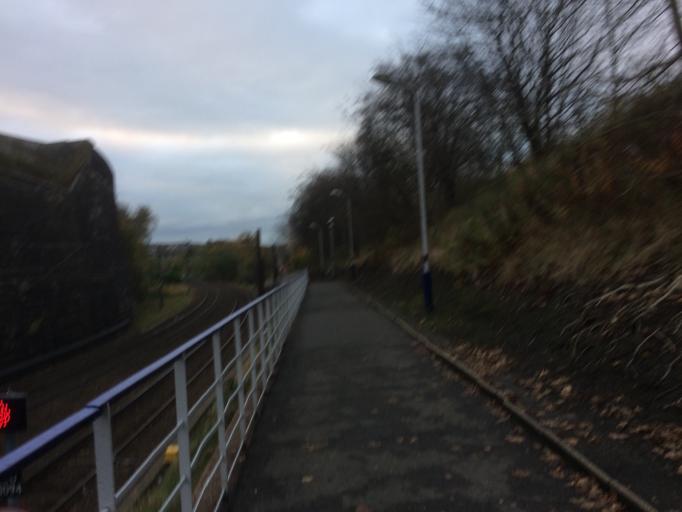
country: GB
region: Scotland
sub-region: Glasgow City
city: Glasgow
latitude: 55.8261
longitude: -4.2613
